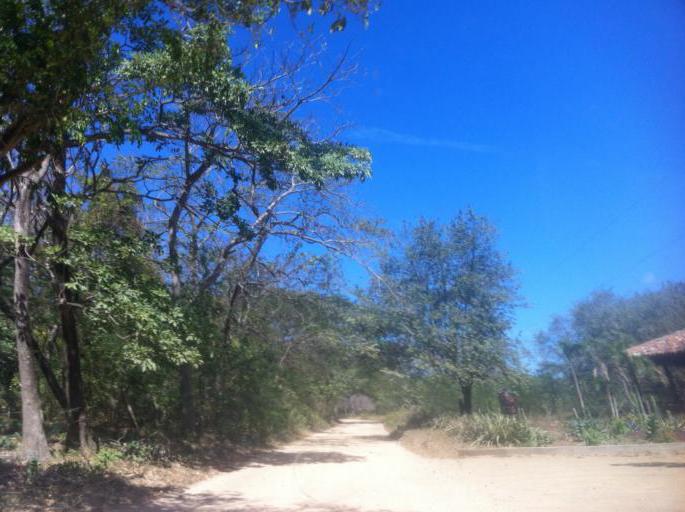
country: NI
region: Rivas
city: Tola
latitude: 11.3851
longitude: -86.0222
